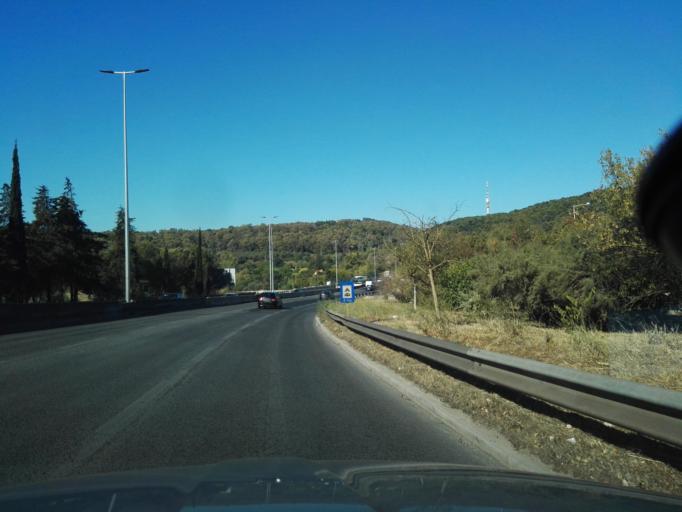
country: PT
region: Lisbon
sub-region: Lisbon
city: Lisbon
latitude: 38.7224
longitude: -9.1711
